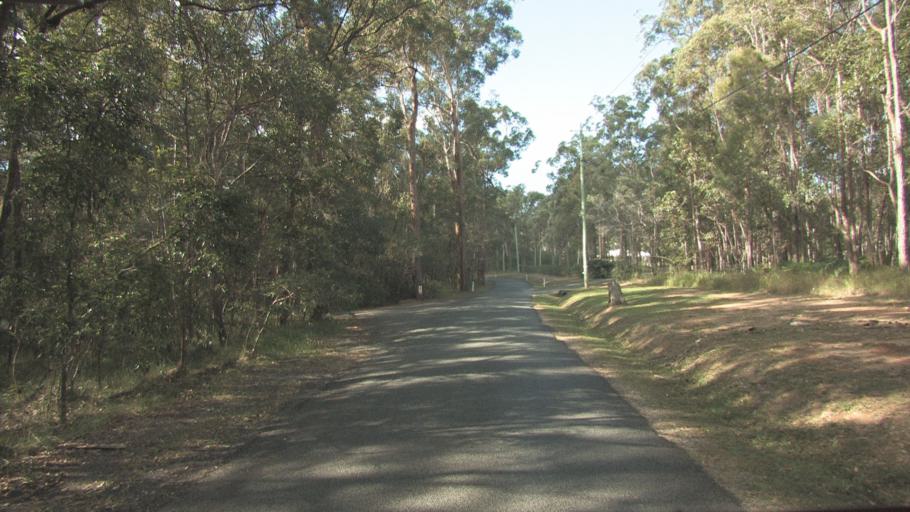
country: AU
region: Queensland
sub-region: Redland
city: Redland Bay
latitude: -27.6546
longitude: 153.2499
